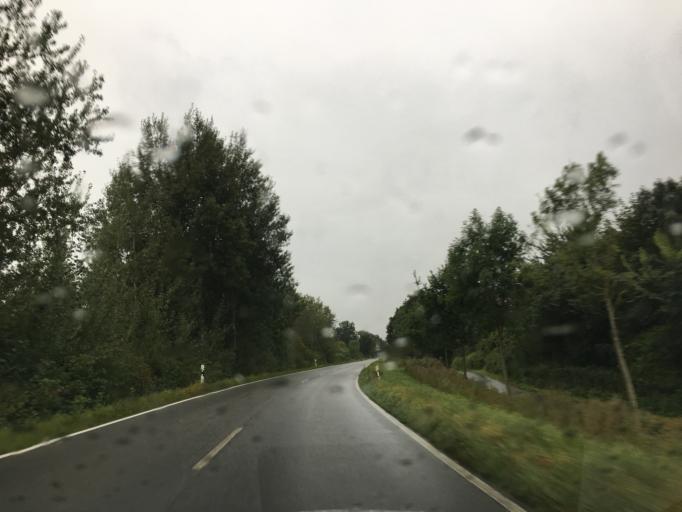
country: DE
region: Schleswig-Holstein
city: Wisch
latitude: 54.4132
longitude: 10.3766
